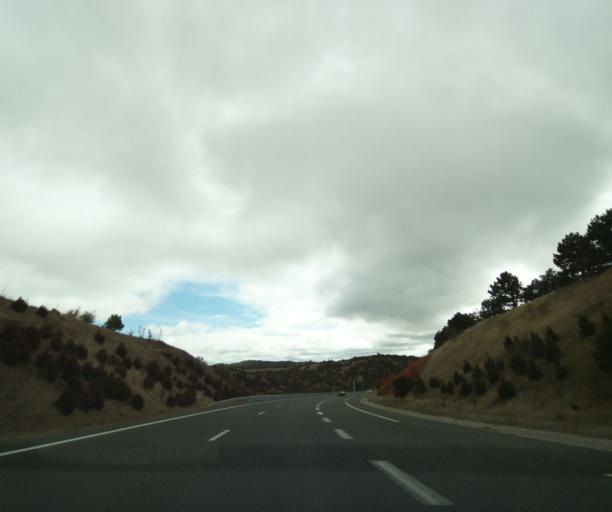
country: FR
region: Languedoc-Roussillon
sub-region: Departement de l'Herault
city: Lodeve
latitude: 43.8454
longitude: 3.3107
